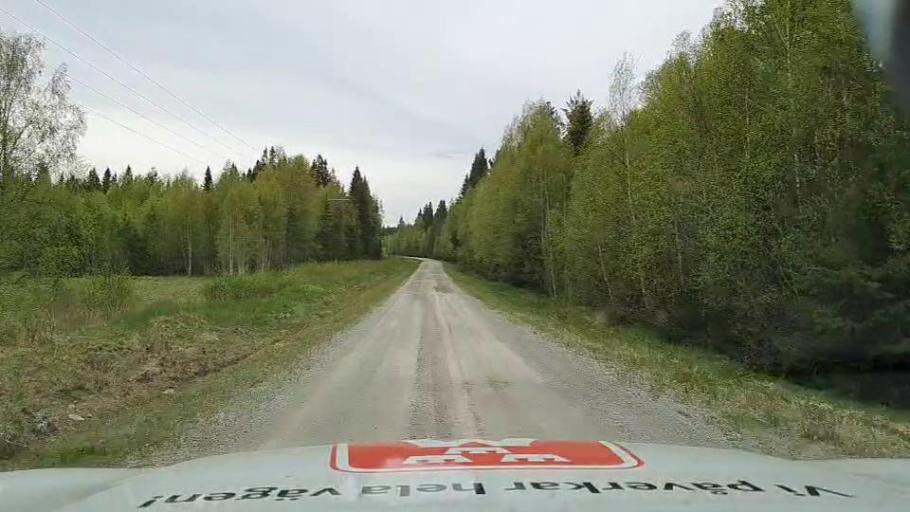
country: SE
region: Jaemtland
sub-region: Bergs Kommun
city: Hoverberg
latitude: 62.6795
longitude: 14.7987
